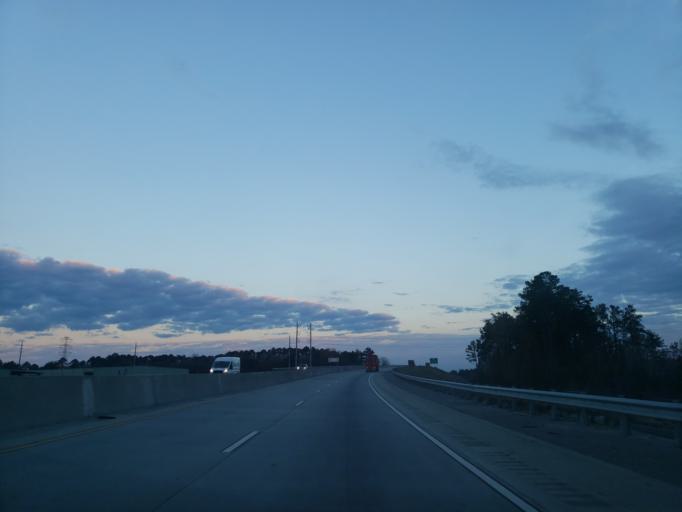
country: US
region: Georgia
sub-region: Chatham County
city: Port Wentworth
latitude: 32.1499
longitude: -81.1749
